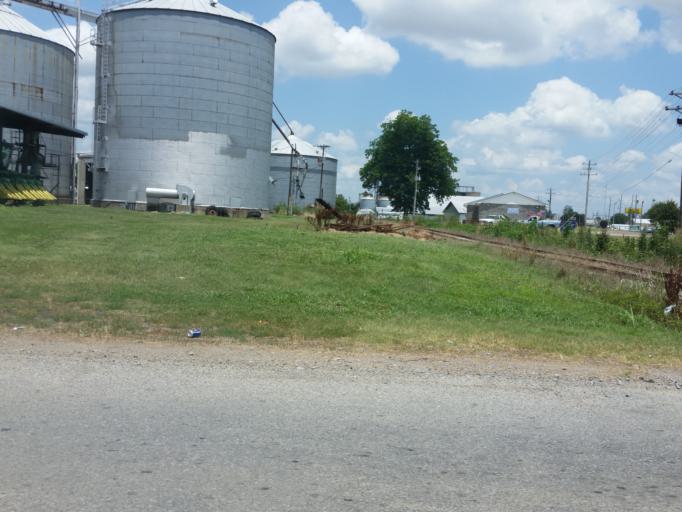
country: US
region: Tennessee
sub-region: Lake County
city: Tiptonville
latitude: 36.3699
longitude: -89.4688
